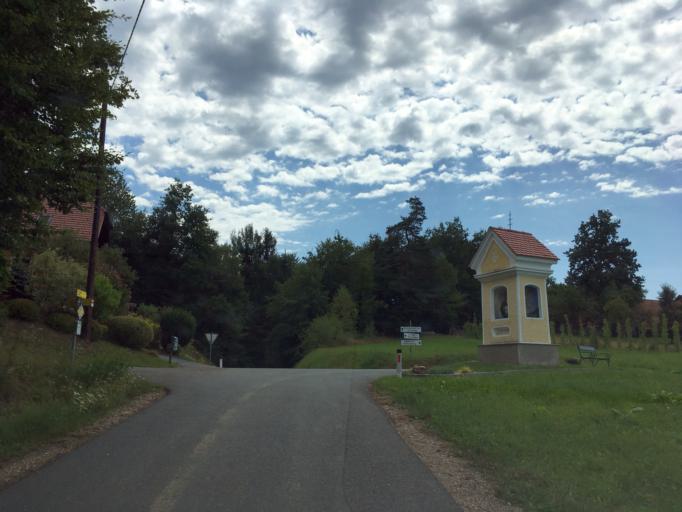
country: AT
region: Styria
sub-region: Politischer Bezirk Leibnitz
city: Kitzeck im Sausal
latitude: 46.7894
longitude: 15.4048
